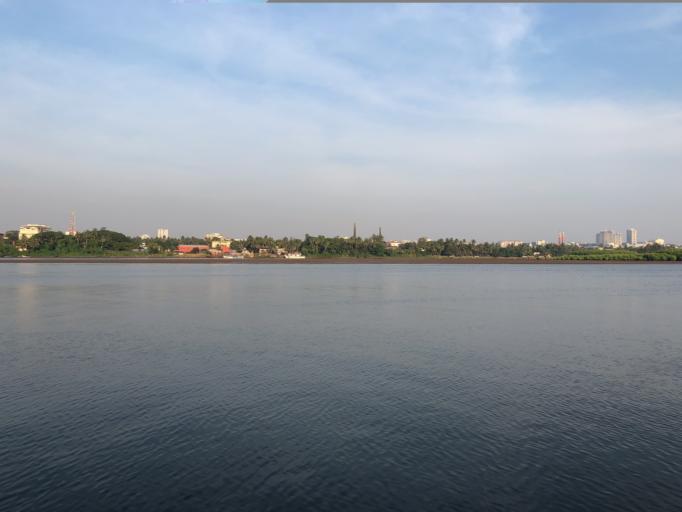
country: IN
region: Karnataka
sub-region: Dakshina Kannada
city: Mangalore
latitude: 12.8803
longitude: 74.8200
